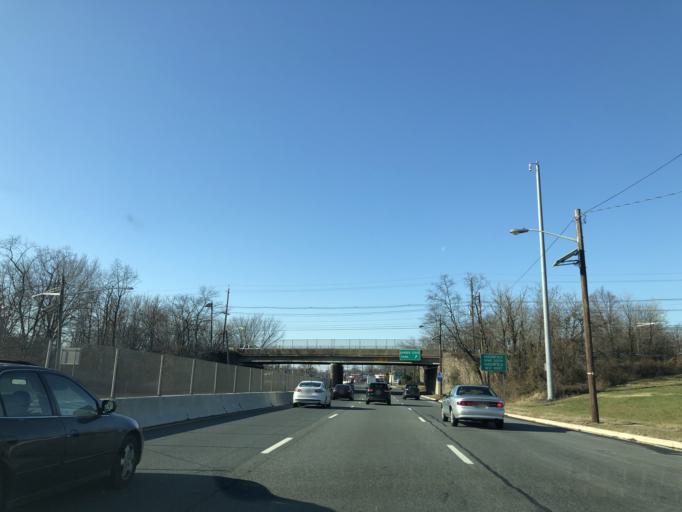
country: US
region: New Jersey
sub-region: Camden County
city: Cherry Hill
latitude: 39.9385
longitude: -75.0289
